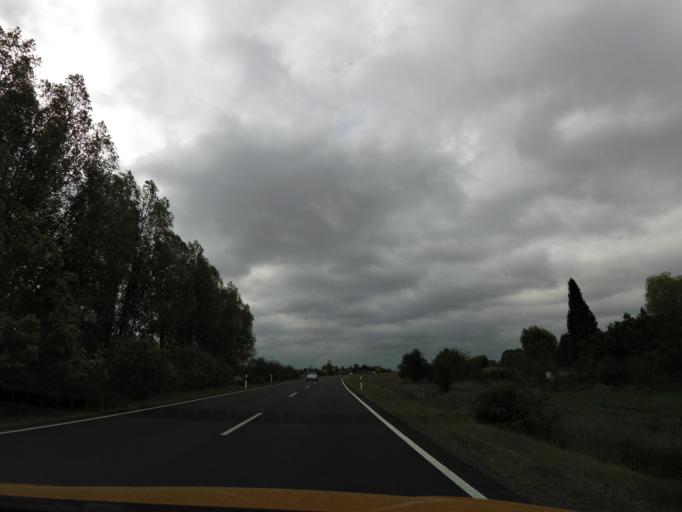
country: DE
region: Brandenburg
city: Beelitz
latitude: 52.2388
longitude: 12.9875
